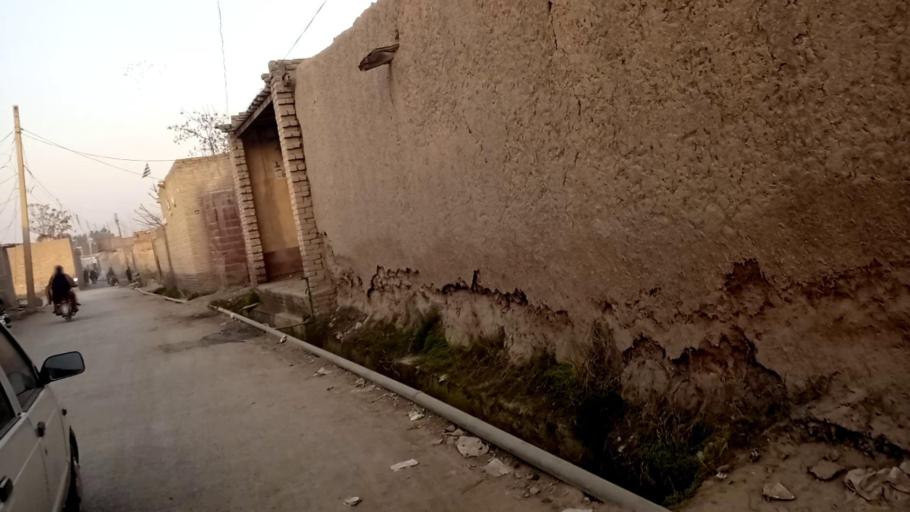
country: PK
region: Khyber Pakhtunkhwa
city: Peshawar
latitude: 34.0484
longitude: 71.4568
